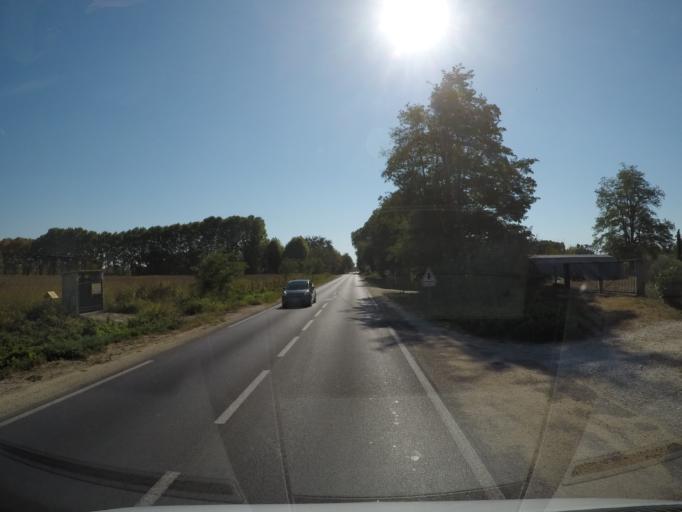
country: FR
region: Languedoc-Roussillon
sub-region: Departement du Gard
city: Moussac
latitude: 43.9728
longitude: 4.2174
